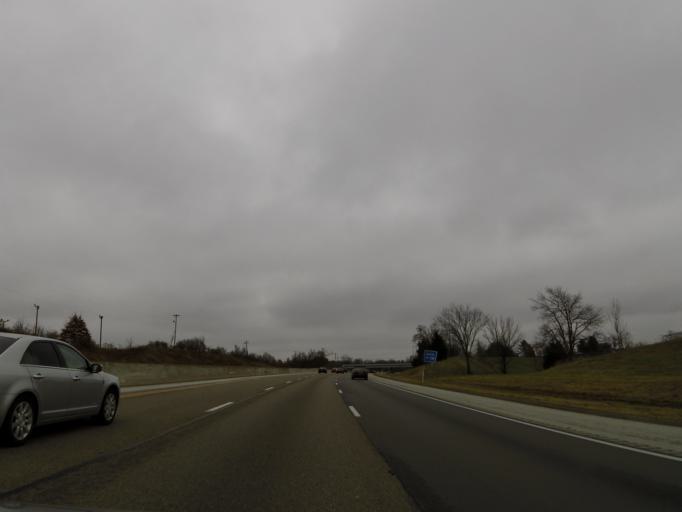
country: US
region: Kentucky
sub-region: Grant County
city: Dry Ridge
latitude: 38.6627
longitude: -84.5881
